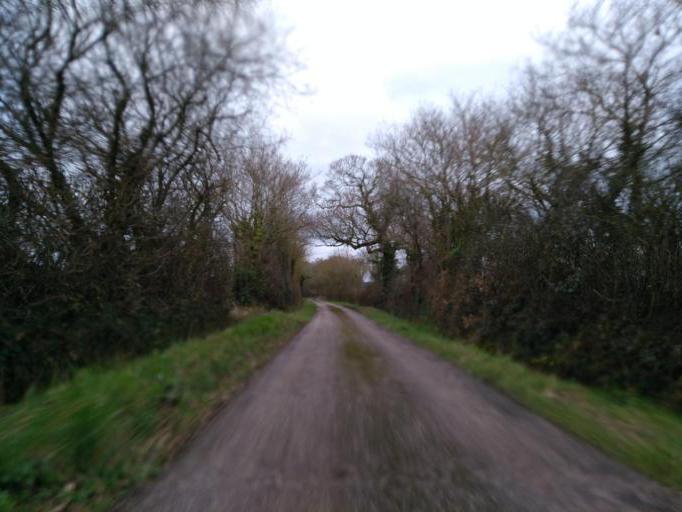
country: GB
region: England
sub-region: Devon
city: Heavitree
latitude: 50.7958
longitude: -3.5005
